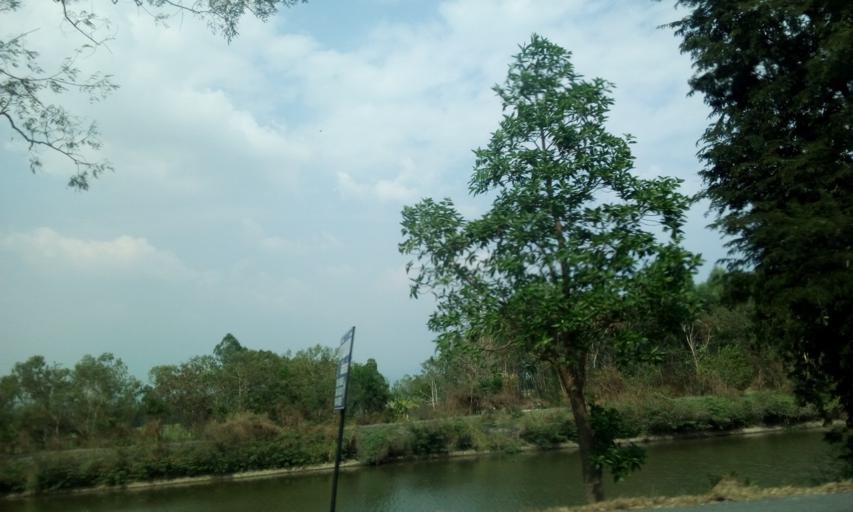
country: TH
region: Nakhon Nayok
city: Nakhon Nayok
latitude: 14.2200
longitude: 101.1545
